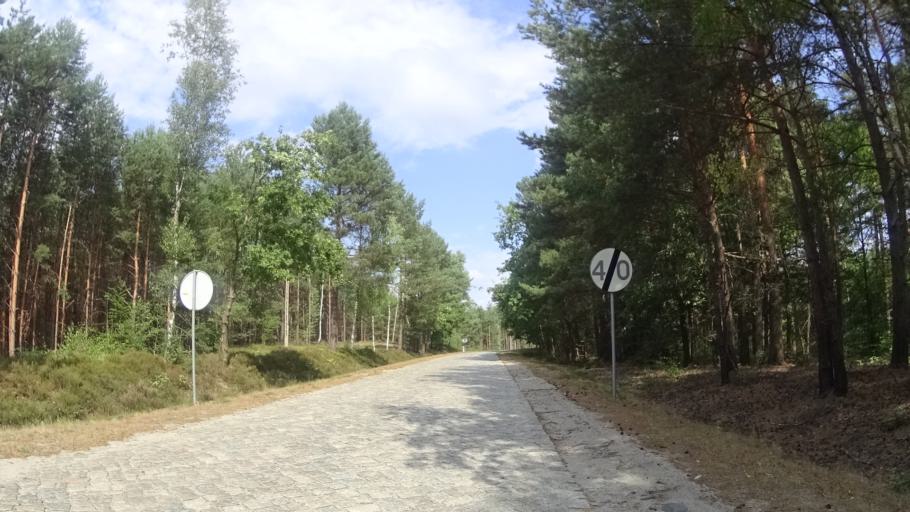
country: PL
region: Lubusz
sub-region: Powiat zarski
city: Leknica
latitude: 51.5266
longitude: 14.8200
